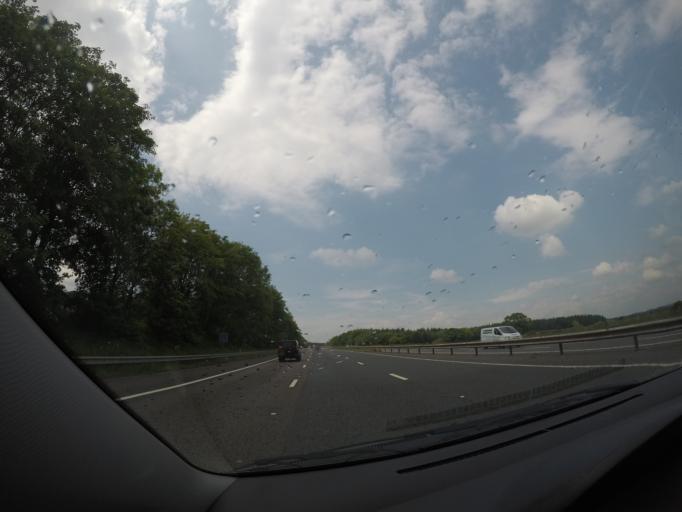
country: GB
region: England
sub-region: Cumbria
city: Penrith
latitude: 54.7602
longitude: -2.8279
